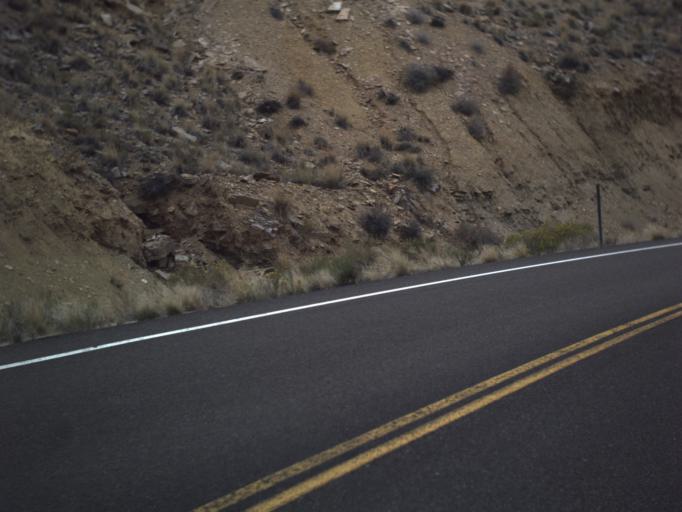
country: US
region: Utah
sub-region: Emery County
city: Castle Dale
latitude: 38.9347
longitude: -110.4767
